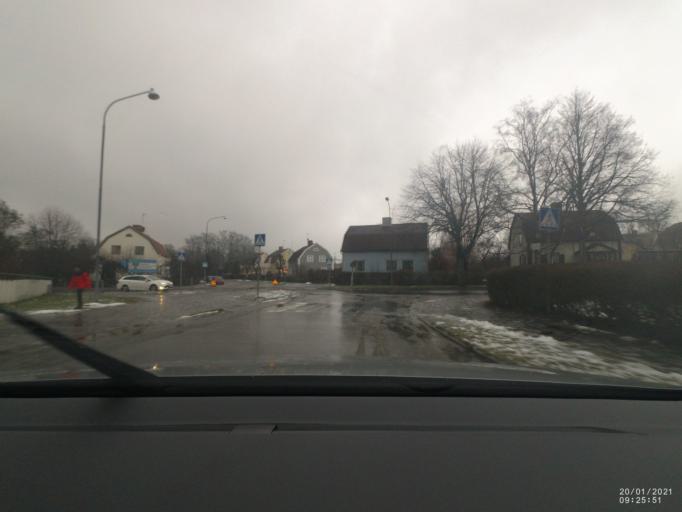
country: SE
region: Soedermanland
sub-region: Nykopings Kommun
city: Nykoping
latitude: 58.7582
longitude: 16.9976
